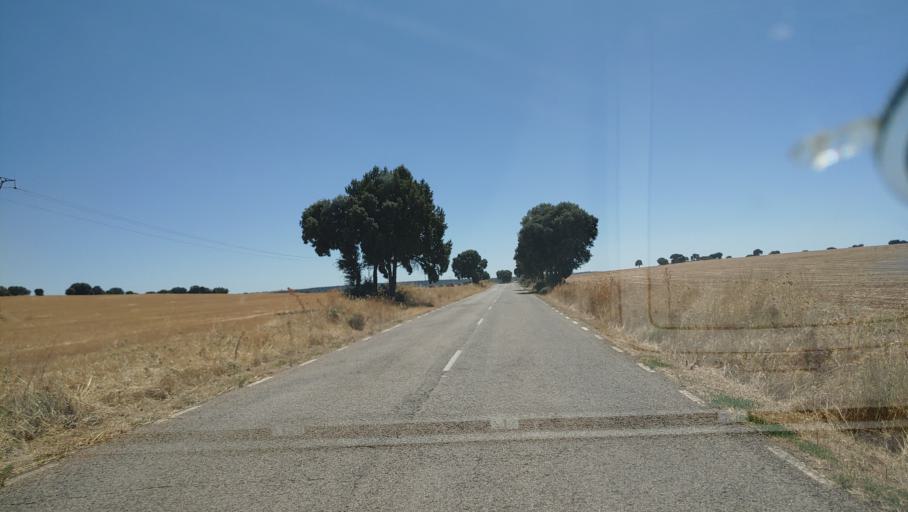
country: ES
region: Castille-La Mancha
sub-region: Provincia de Albacete
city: Ossa de Montiel
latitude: 38.9158
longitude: -2.7585
